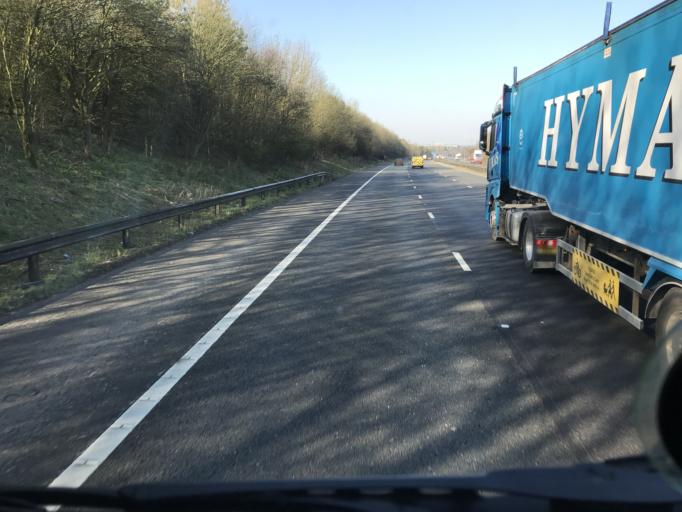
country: GB
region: England
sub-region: Borough of Halton
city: Daresbury
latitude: 53.3286
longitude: -2.6256
